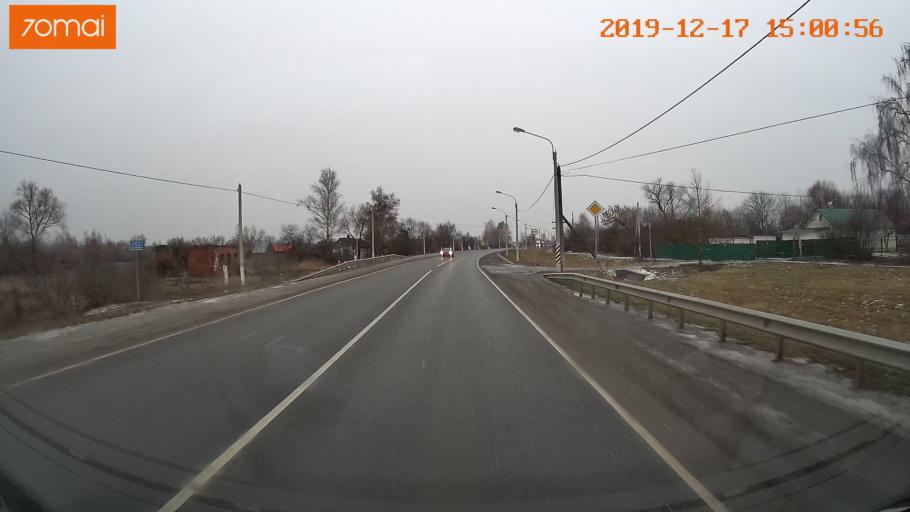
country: RU
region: Rjazan
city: Zakharovo
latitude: 54.2880
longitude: 39.1820
